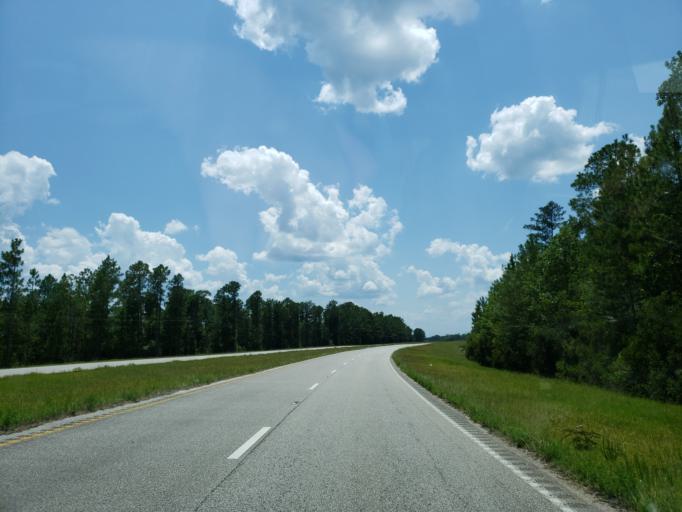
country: US
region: Mississippi
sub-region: Wayne County
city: Belmont
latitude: 31.3690
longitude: -88.4878
